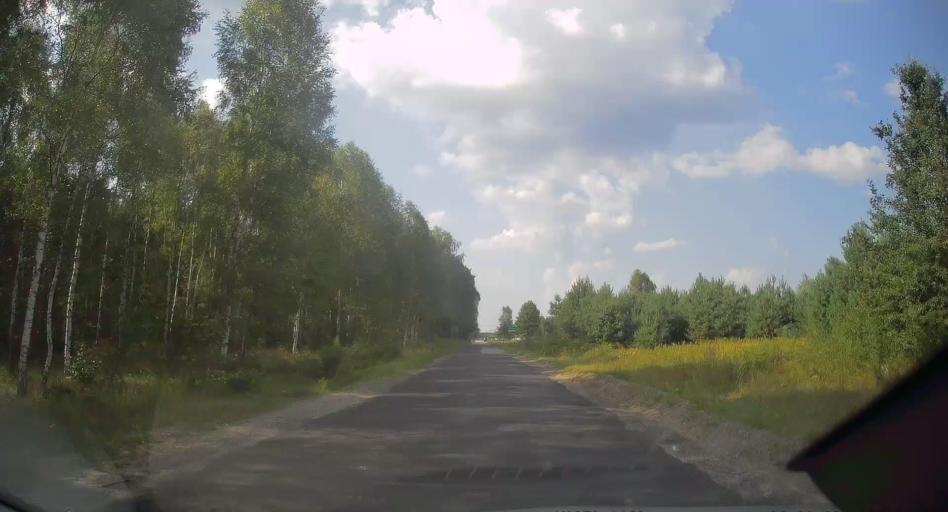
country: PL
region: Swietokrzyskie
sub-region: Powiat konecki
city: Radoszyce
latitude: 51.1095
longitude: 20.2641
